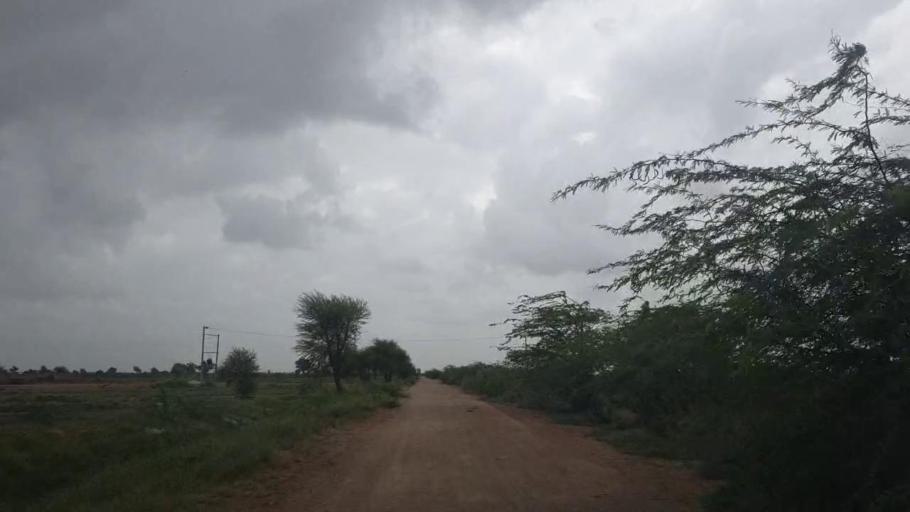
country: PK
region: Sindh
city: Tando Bago
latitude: 24.8459
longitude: 69.1690
